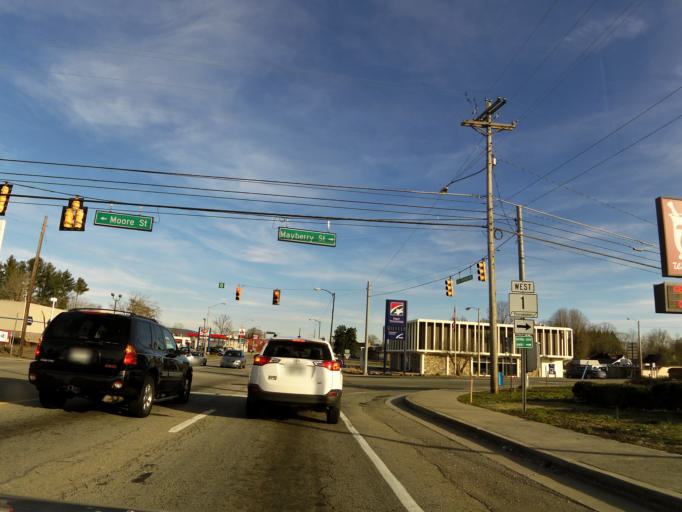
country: US
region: Tennessee
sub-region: White County
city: Sparta
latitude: 35.9320
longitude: -85.4767
